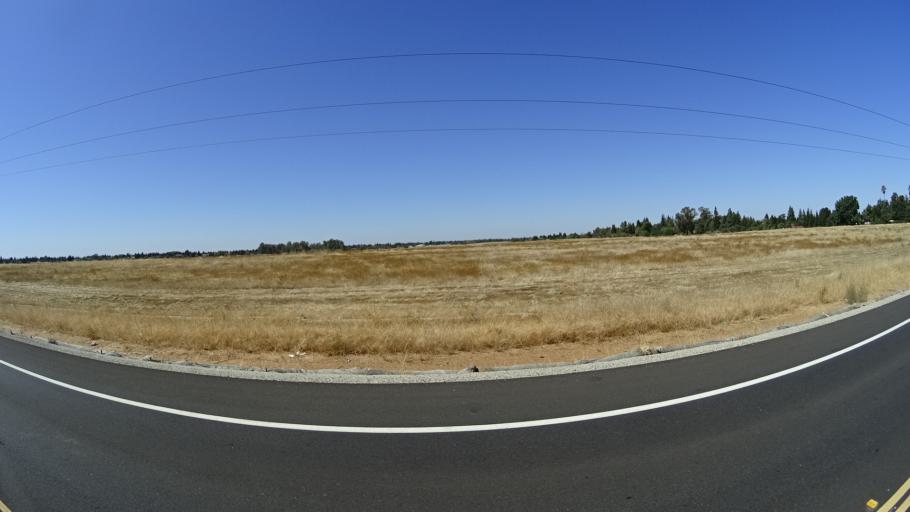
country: US
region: California
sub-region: Sacramento County
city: Elk Grove
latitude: 38.4325
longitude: -121.3532
